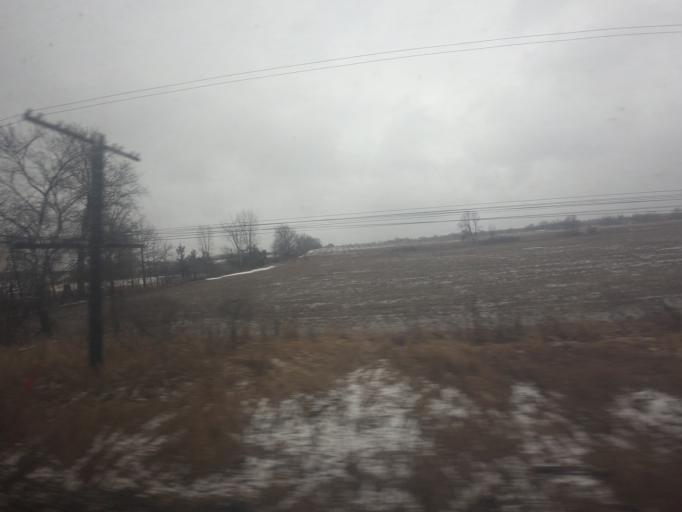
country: CA
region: Ontario
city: Deseronto
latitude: 44.2263
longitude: -77.0601
